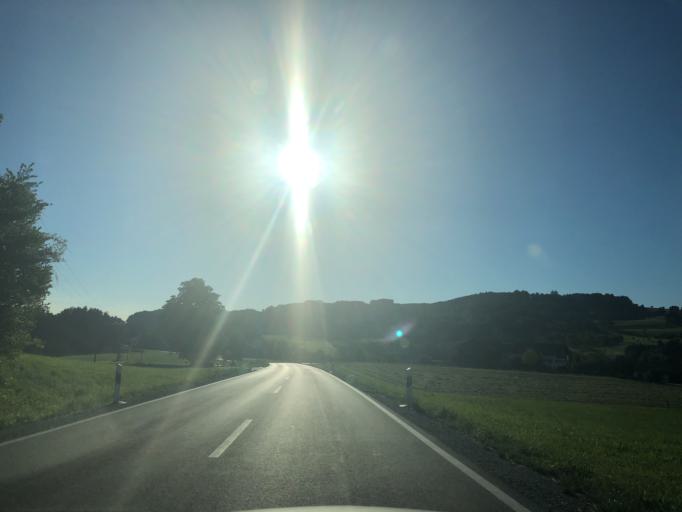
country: DE
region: Bavaria
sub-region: Upper Bavaria
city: Rimsting
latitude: 47.8623
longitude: 12.3148
